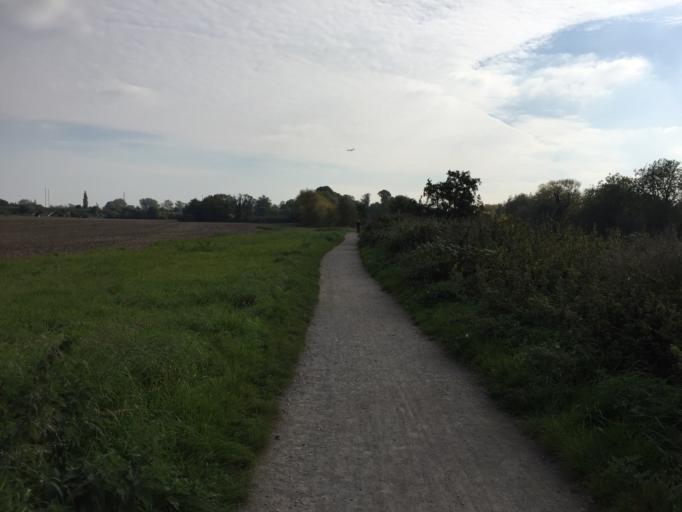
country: GB
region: England
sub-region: West Berkshire
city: Eton
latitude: 51.4921
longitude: -0.6289
